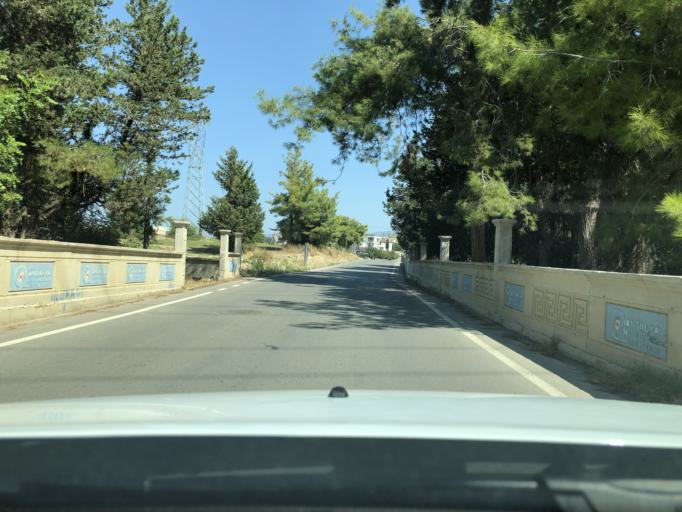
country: TR
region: Antalya
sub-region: Manavgat
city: Manavgat
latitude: 36.8163
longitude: 31.4888
